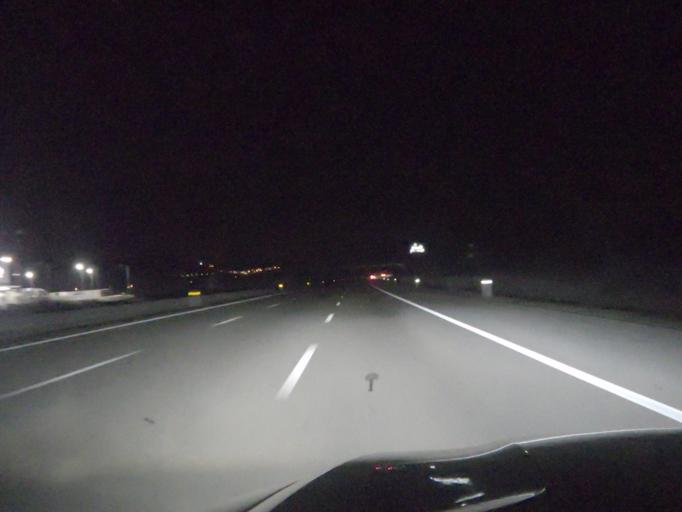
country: PT
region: Santarem
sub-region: Alcanena
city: Alcanena
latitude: 39.4434
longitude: -8.6292
